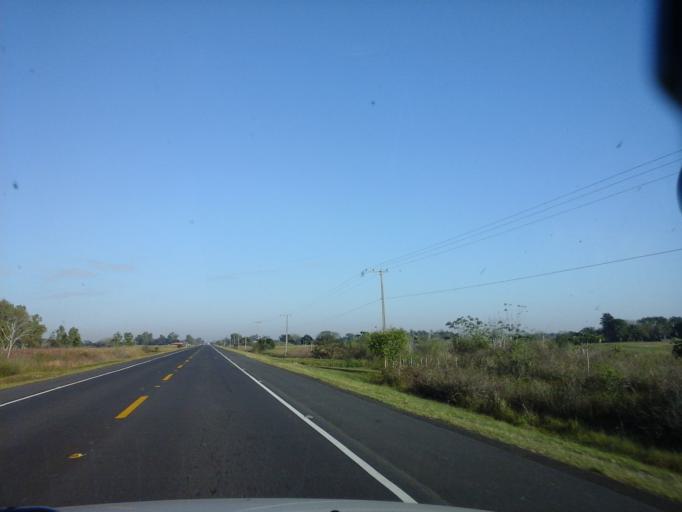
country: PY
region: Neembucu
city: Pilar
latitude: -26.8577
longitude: -58.0110
